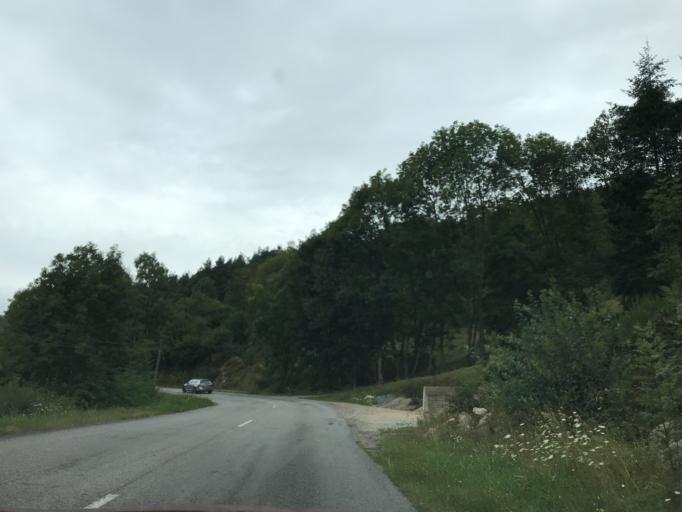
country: FR
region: Rhone-Alpes
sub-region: Departement de la Loire
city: Sail-sous-Couzan
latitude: 45.6988
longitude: 3.8772
